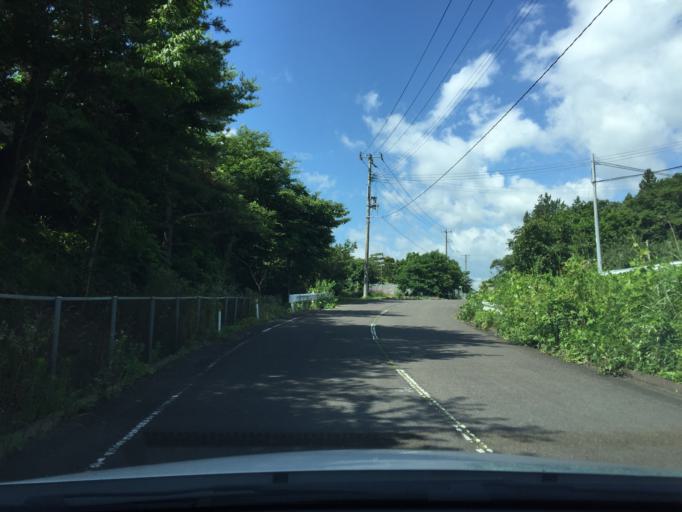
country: JP
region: Fukushima
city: Nihommatsu
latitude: 37.6649
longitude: 140.4500
